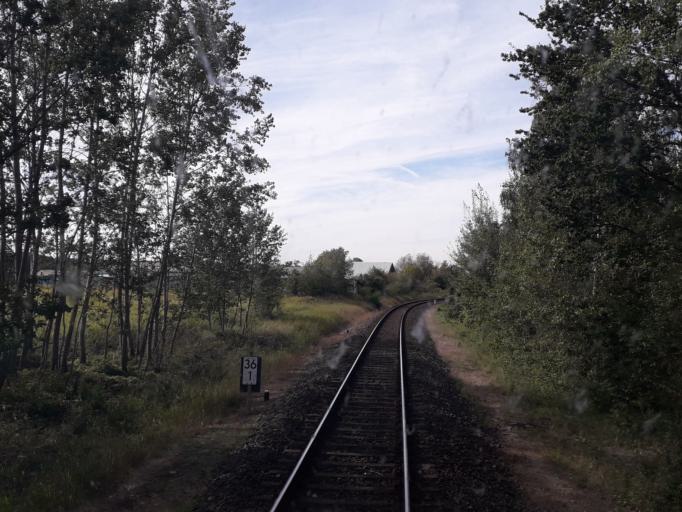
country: DE
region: Brandenburg
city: Kremmen
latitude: 52.7466
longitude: 13.0517
